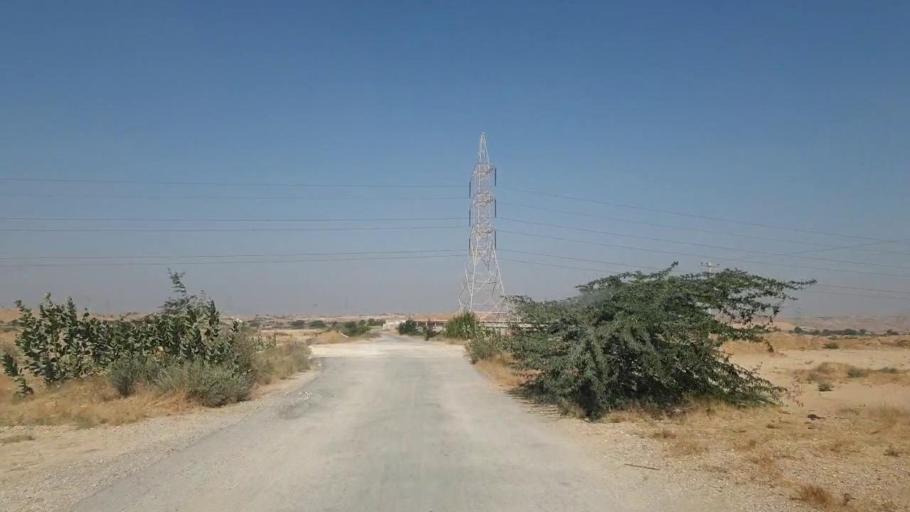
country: PK
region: Sindh
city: Thatta
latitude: 25.1872
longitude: 67.8042
